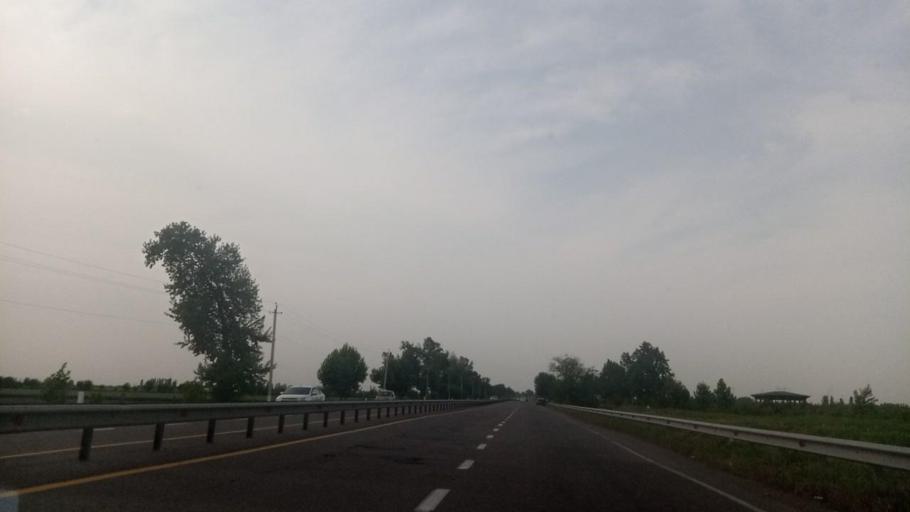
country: UZ
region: Toshkent Shahri
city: Bektemir
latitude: 41.1692
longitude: 69.4150
